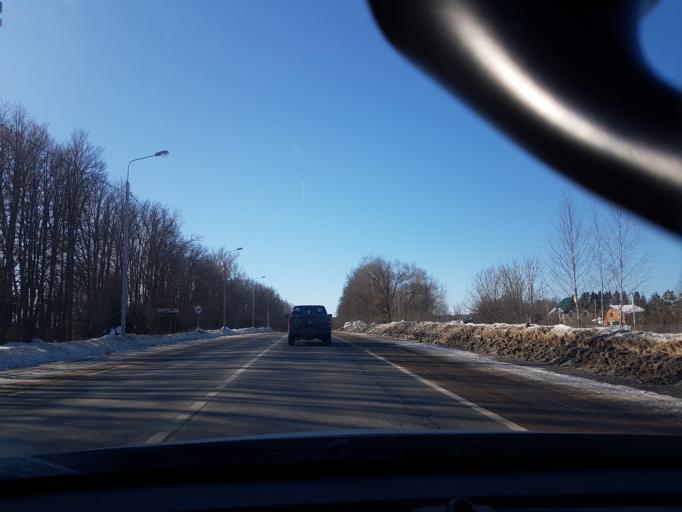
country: RU
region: Moskovskaya
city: Kostrovo
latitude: 55.9176
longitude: 36.6776
